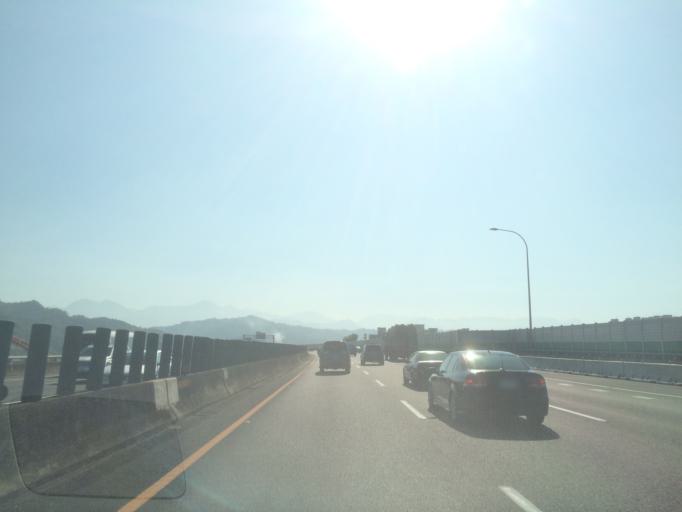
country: TW
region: Taiwan
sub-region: Nantou
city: Nantou
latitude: 23.9163
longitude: 120.6914
